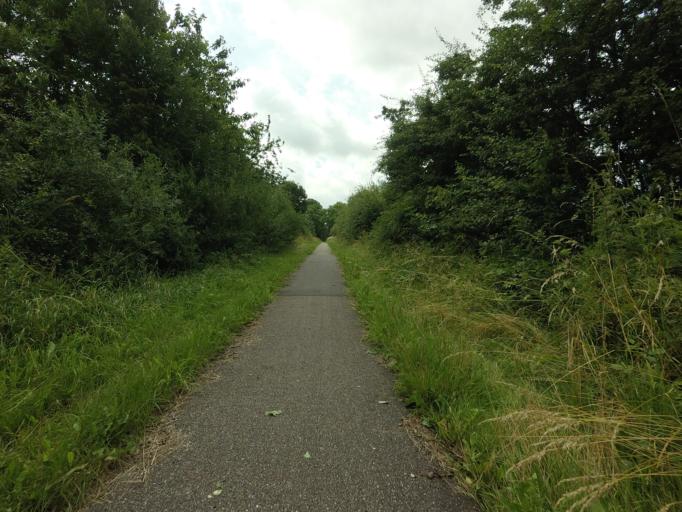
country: DK
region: Central Jutland
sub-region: Randers Kommune
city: Langa
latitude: 56.3288
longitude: 9.8919
